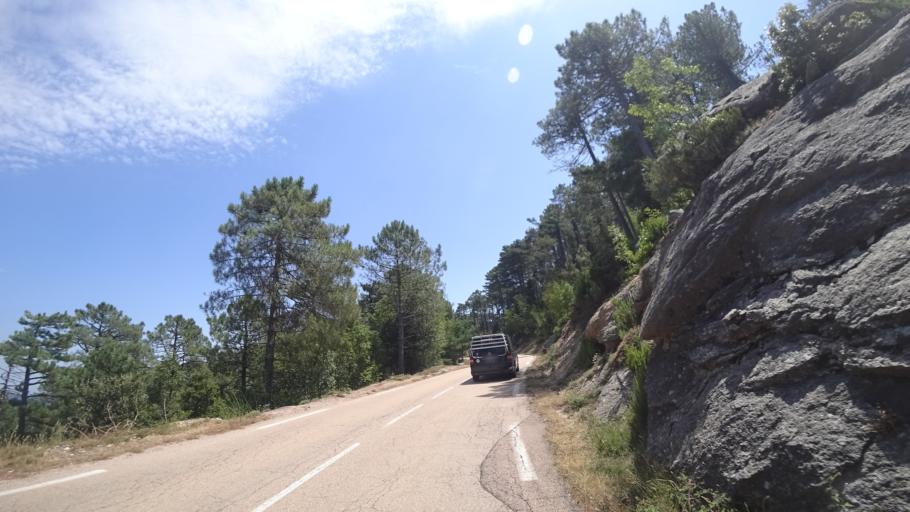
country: FR
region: Corsica
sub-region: Departement de la Corse-du-Sud
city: Zonza
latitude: 41.6769
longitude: 9.2039
